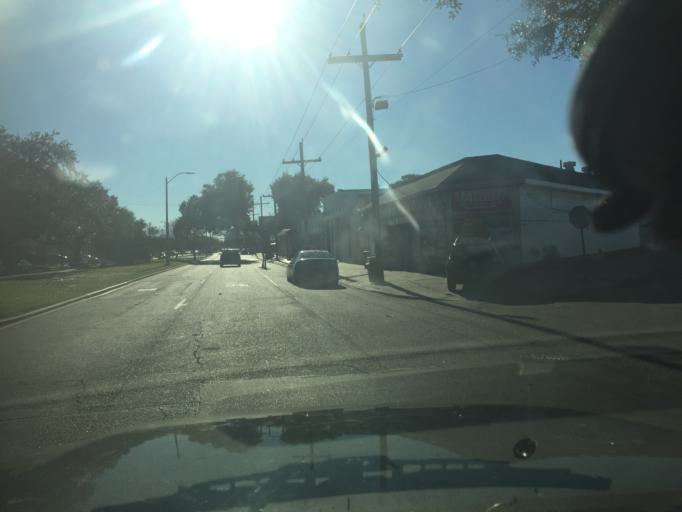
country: US
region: Louisiana
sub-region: Orleans Parish
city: New Orleans
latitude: 29.9851
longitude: -90.0703
